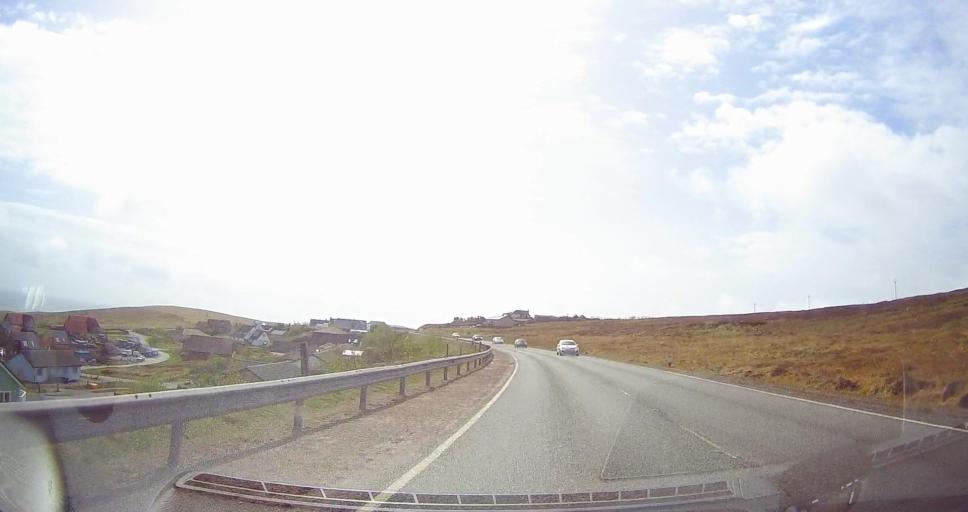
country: GB
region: Scotland
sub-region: Shetland Islands
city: Lerwick
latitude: 60.1250
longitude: -1.2170
